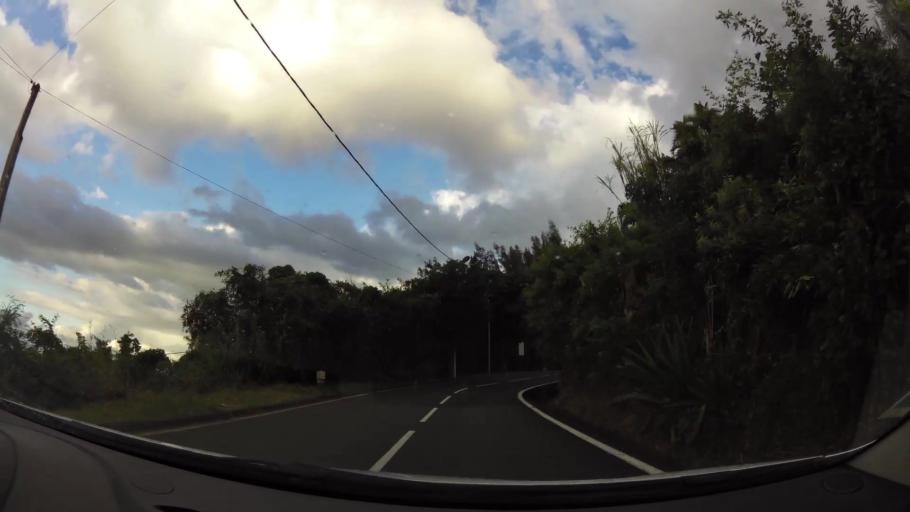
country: RE
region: Reunion
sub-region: Reunion
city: Saint-Denis
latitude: -20.9067
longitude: 55.4444
